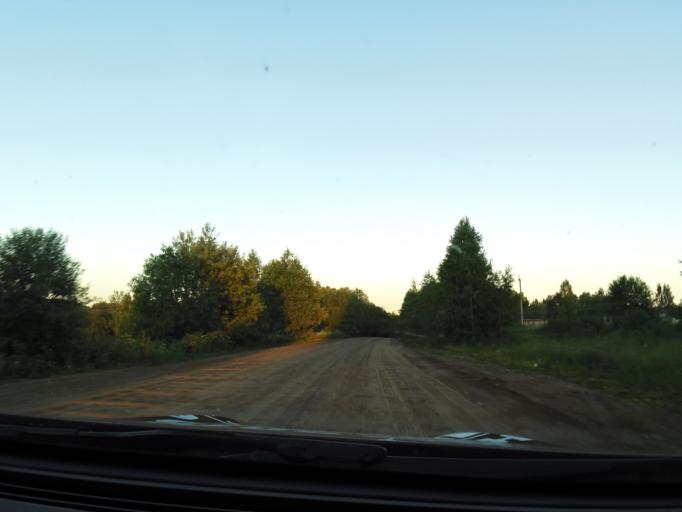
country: RU
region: Leningrad
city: Voznesen'ye
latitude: 60.9051
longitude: 35.5012
